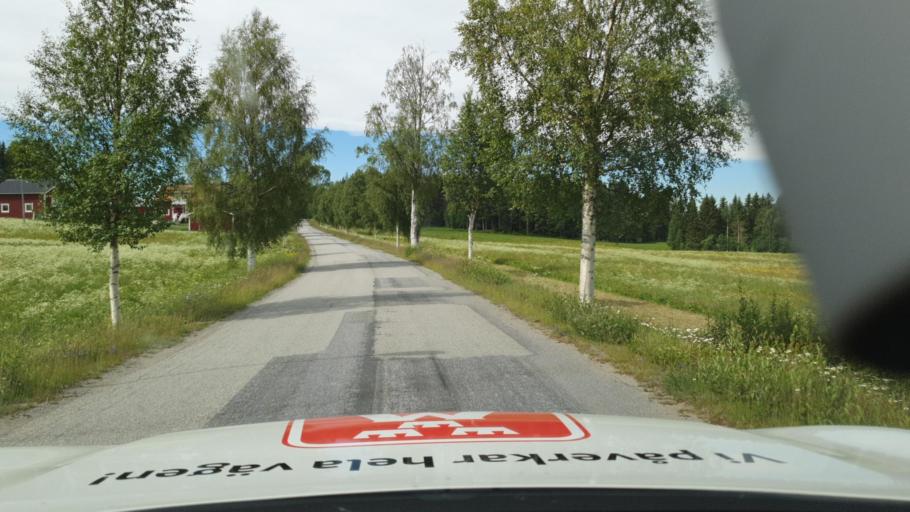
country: SE
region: Vaesterbotten
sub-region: Skelleftea Kommun
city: Burtraesk
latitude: 64.4288
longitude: 20.5259
